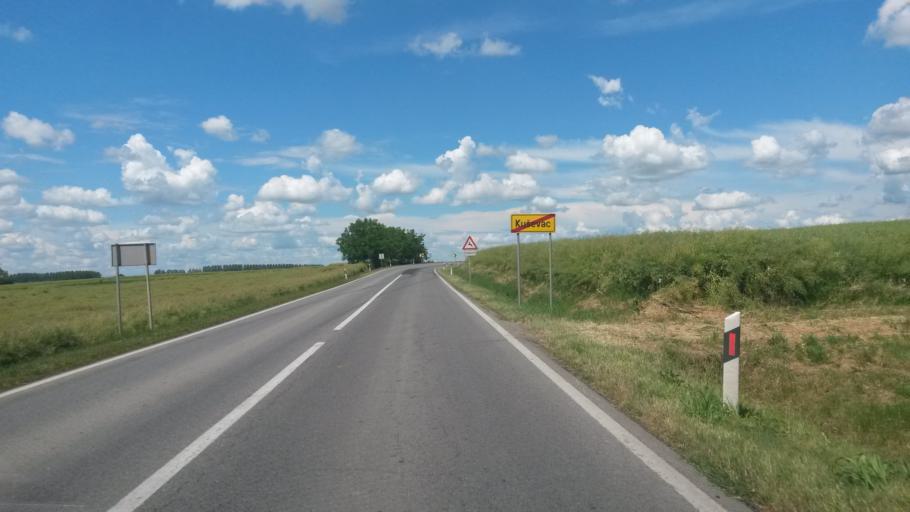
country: HR
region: Osjecko-Baranjska
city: Viskovci
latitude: 45.3590
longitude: 18.4258
